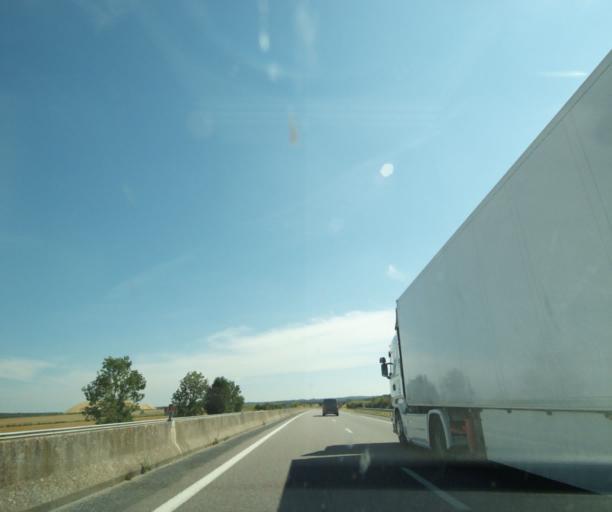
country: FR
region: Lorraine
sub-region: Departement de Meurthe-et-Moselle
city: Colombey-les-Belles
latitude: 48.4728
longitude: 5.8817
